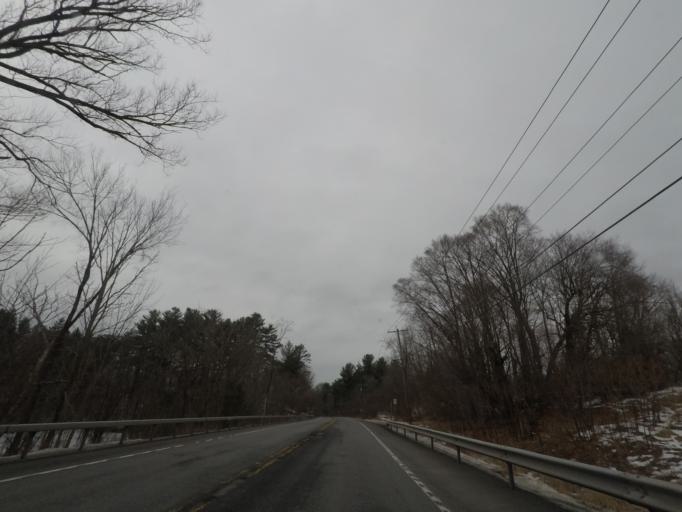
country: US
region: New York
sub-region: Schenectady County
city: Rotterdam
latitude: 42.7306
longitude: -73.9736
